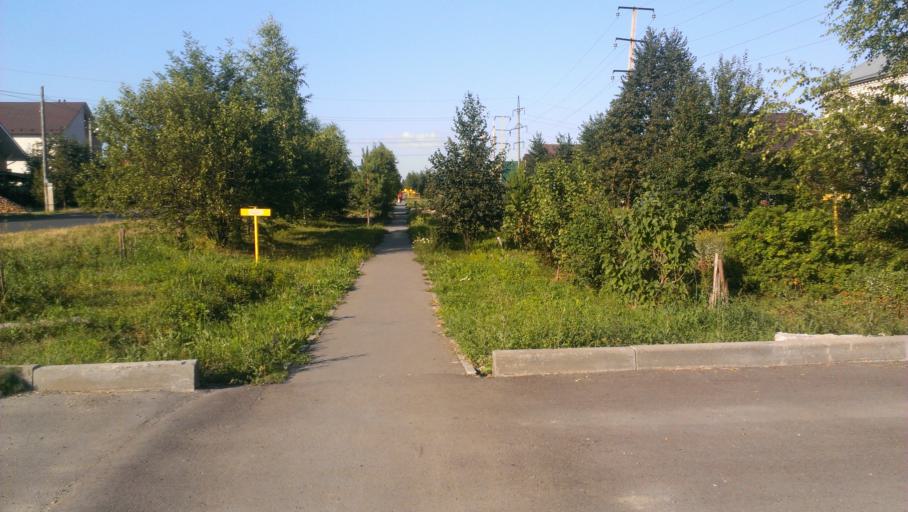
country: RU
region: Altai Krai
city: Novosilikatnyy
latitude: 53.3573
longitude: 83.6376
